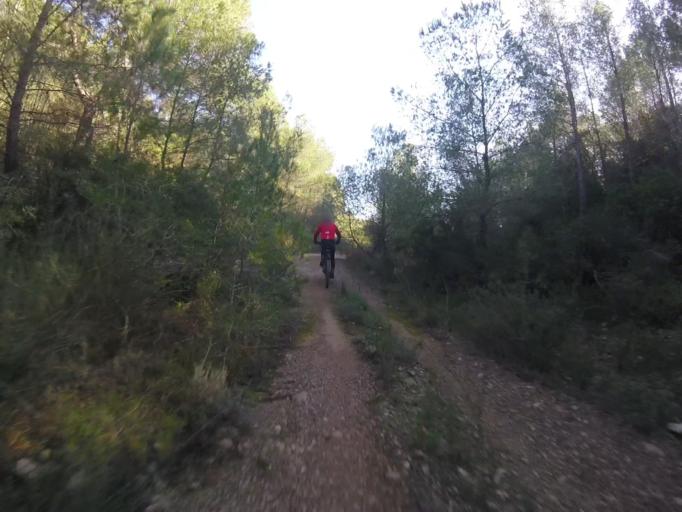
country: ES
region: Valencia
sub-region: Provincia de Castello
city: Santa Magdalena de Pulpis
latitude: 40.3074
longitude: 0.3357
